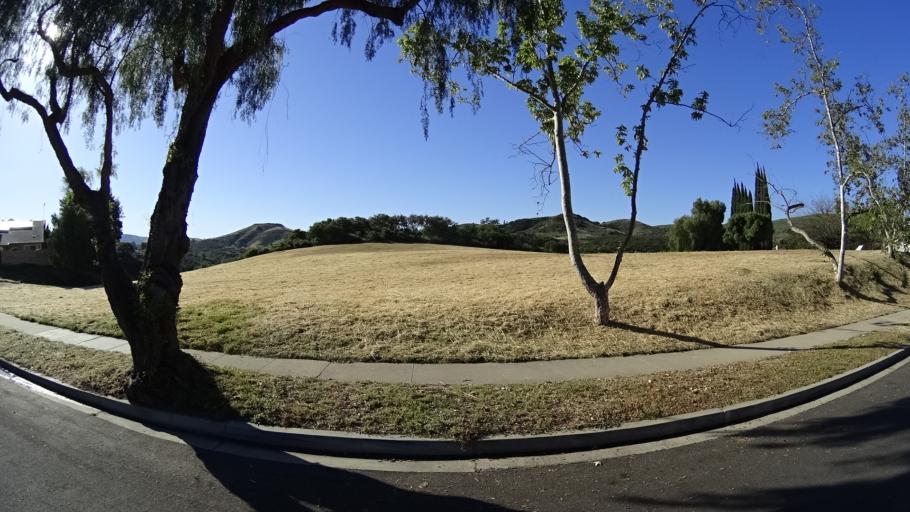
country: US
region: California
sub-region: Ventura County
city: Casa Conejo
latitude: 34.2153
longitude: -118.8989
